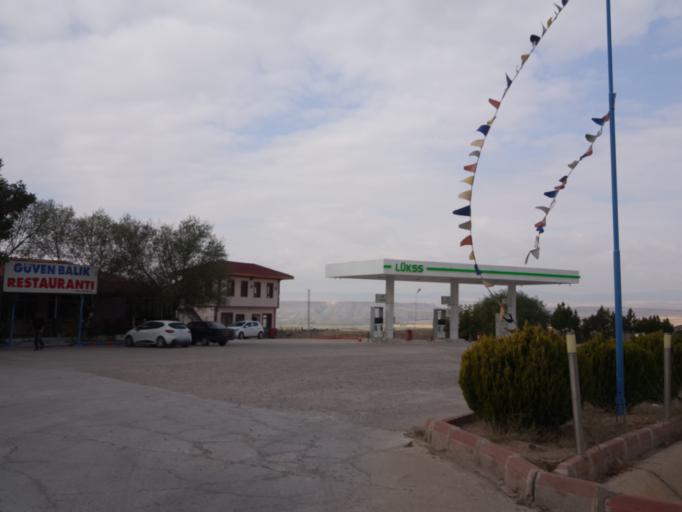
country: TR
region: Kirikkale
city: Karakecili
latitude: 39.5519
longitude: 33.4501
